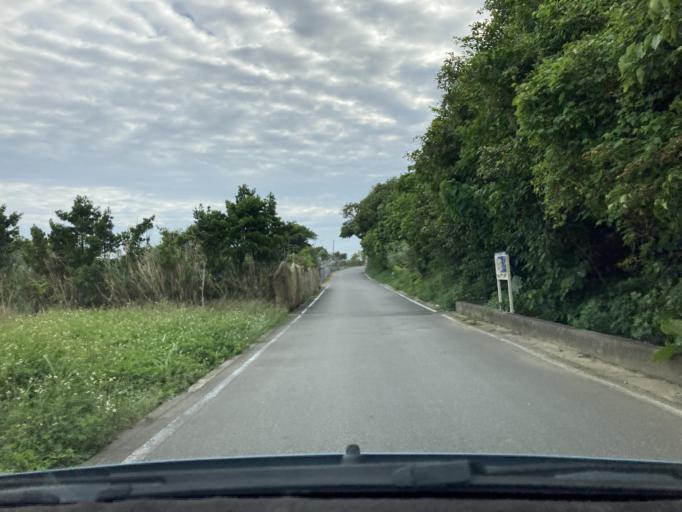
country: JP
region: Okinawa
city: Tomigusuku
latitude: 26.1364
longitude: 127.7928
